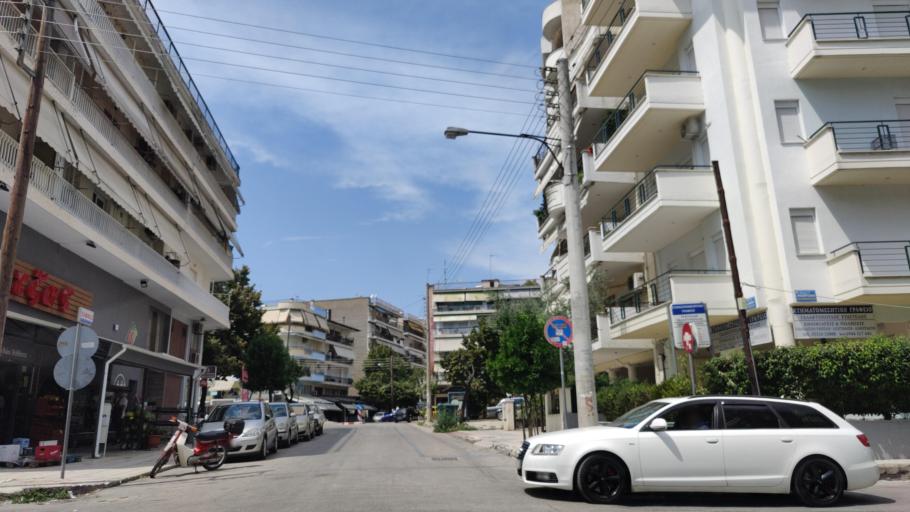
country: GR
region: Central Macedonia
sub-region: Nomos Serron
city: Serres
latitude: 41.0861
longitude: 23.5422
